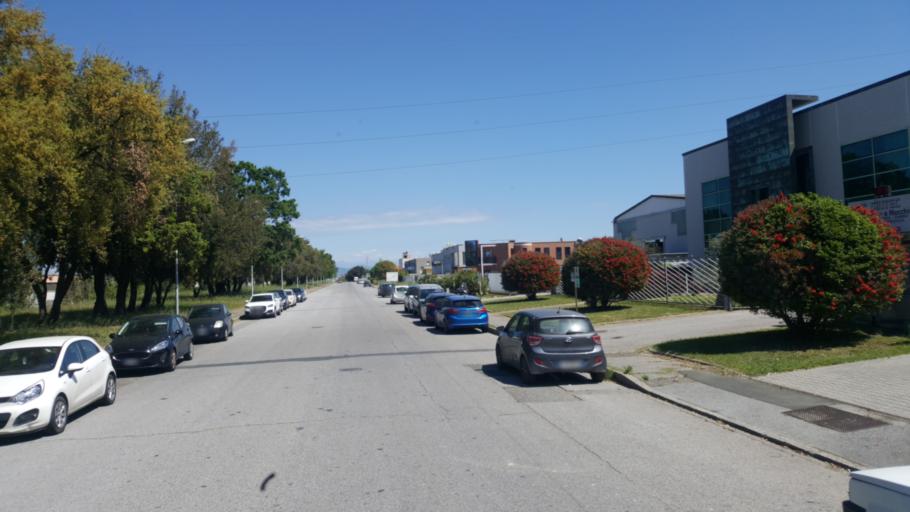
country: IT
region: Tuscany
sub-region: Provincia di Livorno
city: Livorno
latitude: 43.5708
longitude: 10.3425
